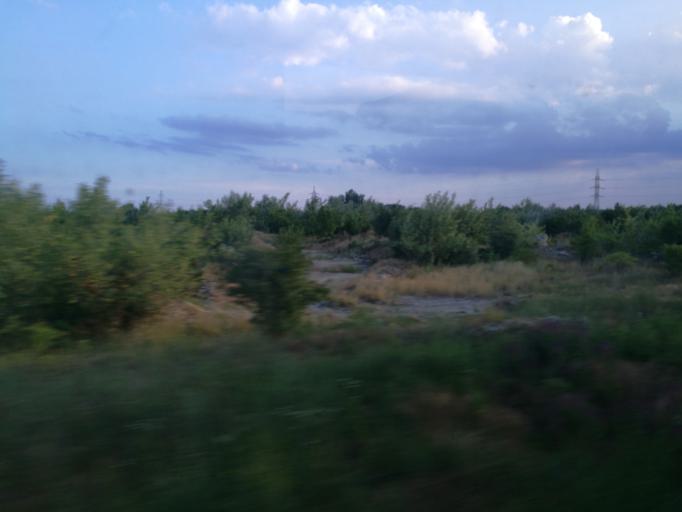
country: RO
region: Dambovita
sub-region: Comuna Titu
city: Salcuta
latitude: 44.6615
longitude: 25.5818
